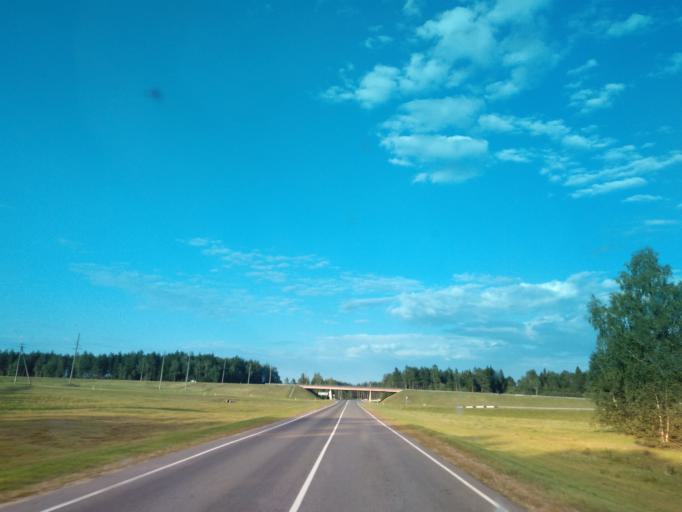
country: BY
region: Minsk
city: Uzda
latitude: 53.4364
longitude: 27.4888
